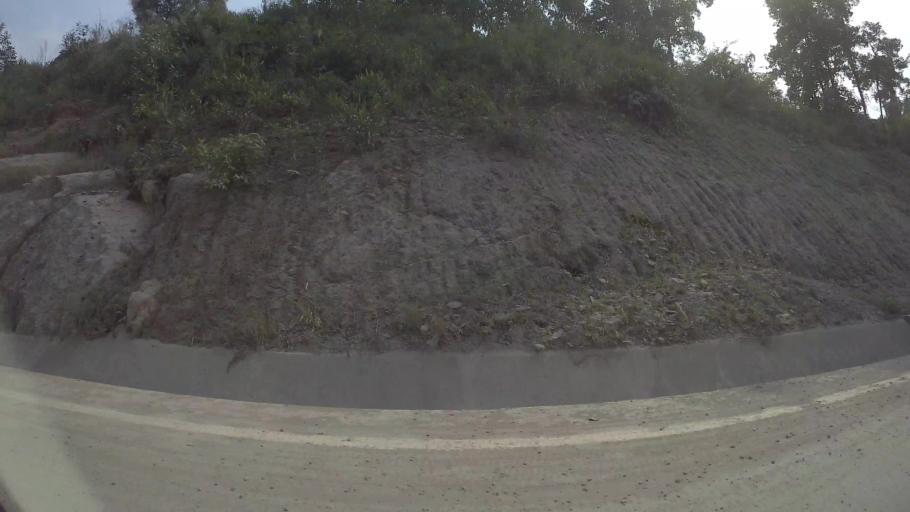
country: VN
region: Da Nang
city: Lien Chieu
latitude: 16.0422
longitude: 108.1635
